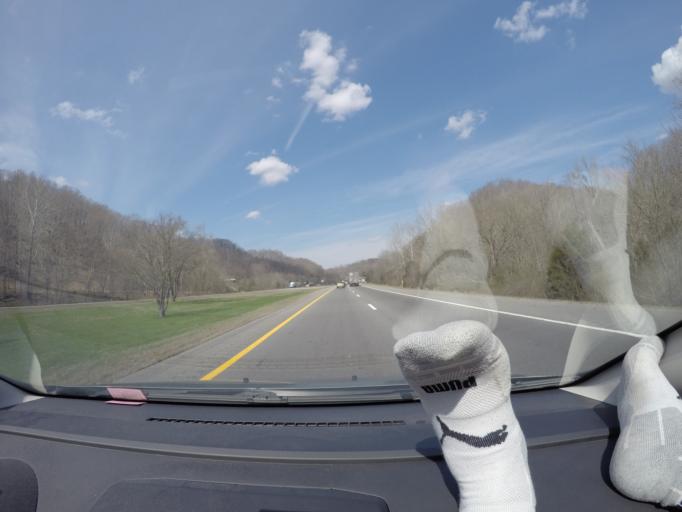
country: US
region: Tennessee
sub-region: Robertson County
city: Ridgetop
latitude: 36.3125
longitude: -86.8290
